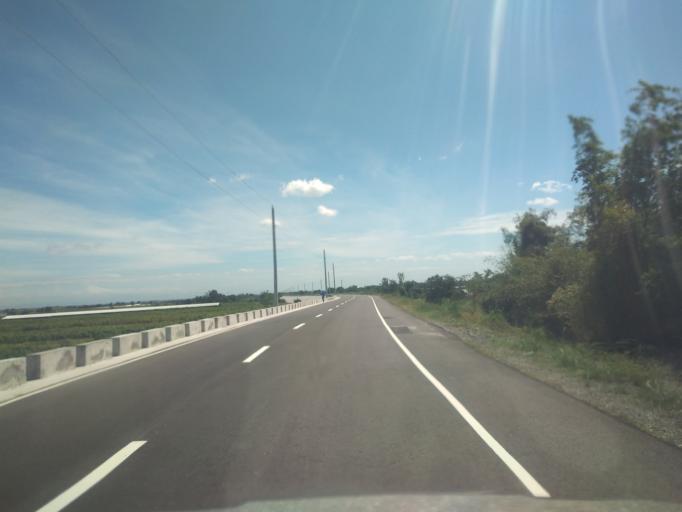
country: PH
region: Central Luzon
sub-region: Province of Pampanga
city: Pulung Santol
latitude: 15.0588
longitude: 120.5676
